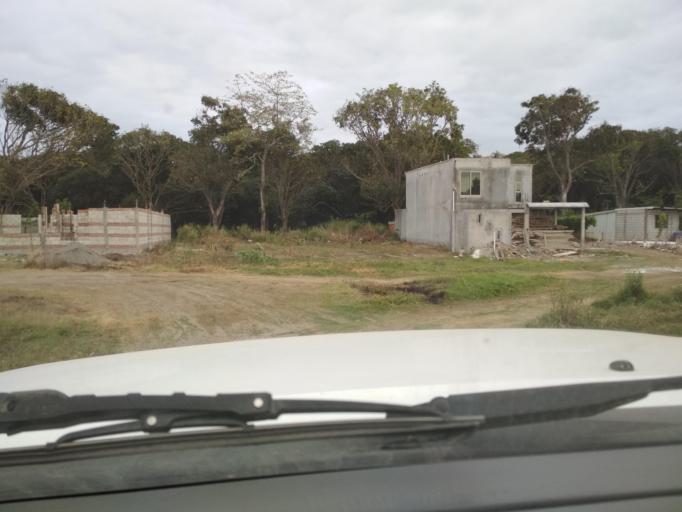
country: MX
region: Veracruz
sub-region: Medellin
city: Fraccionamiento Arboledas San Ramon
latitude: 19.0829
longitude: -96.1512
